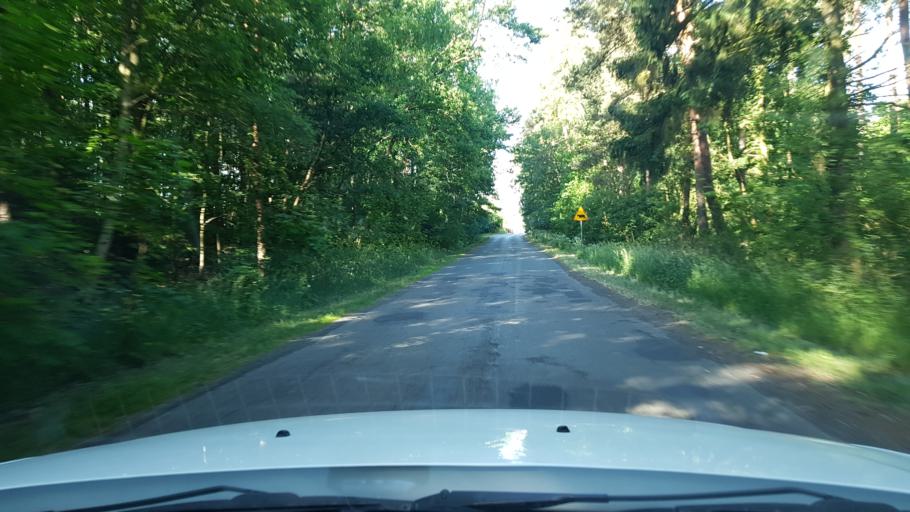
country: PL
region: West Pomeranian Voivodeship
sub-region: Powiat pyrzycki
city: Bielice
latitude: 53.2230
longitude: 14.6206
